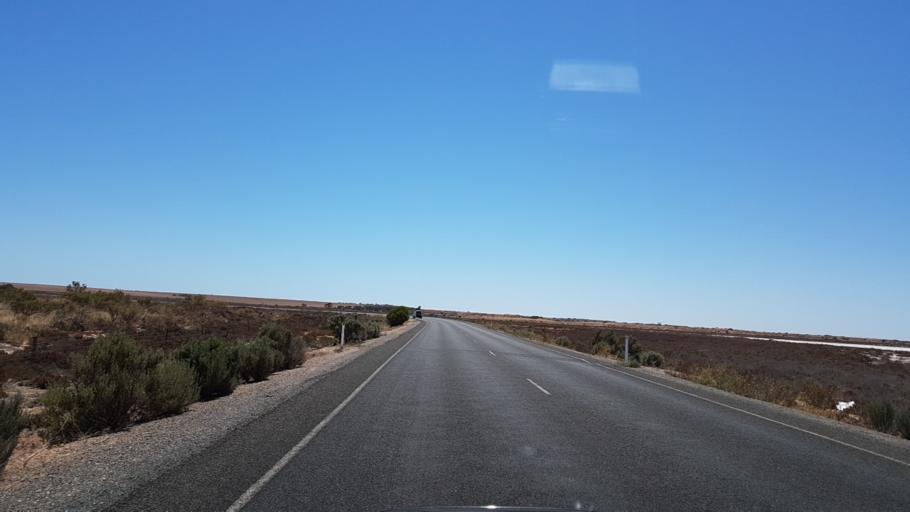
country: AU
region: South Australia
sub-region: Copper Coast
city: Wallaroo
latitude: -33.9175
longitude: 137.6462
